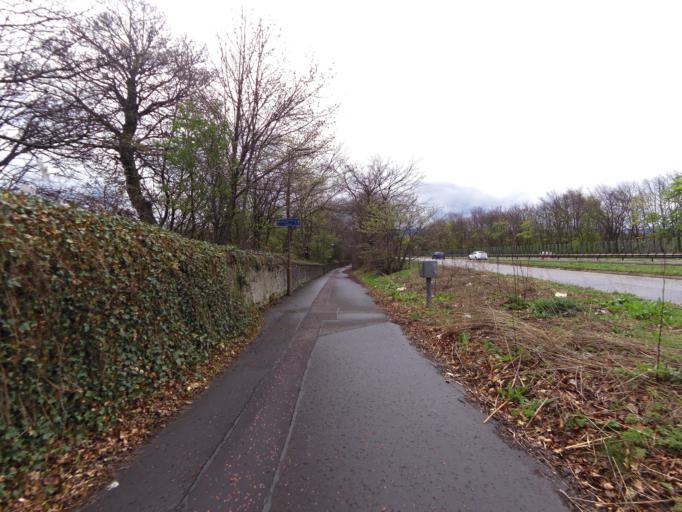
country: GB
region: Scotland
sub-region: Edinburgh
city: Currie
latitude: 55.9676
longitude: -3.3208
